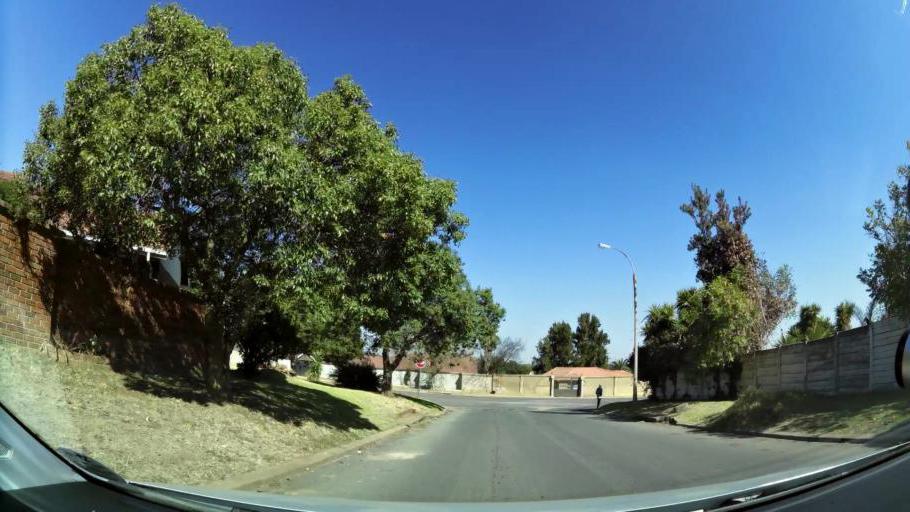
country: ZA
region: Gauteng
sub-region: Ekurhuleni Metropolitan Municipality
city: Tembisa
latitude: -26.0360
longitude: 28.2315
